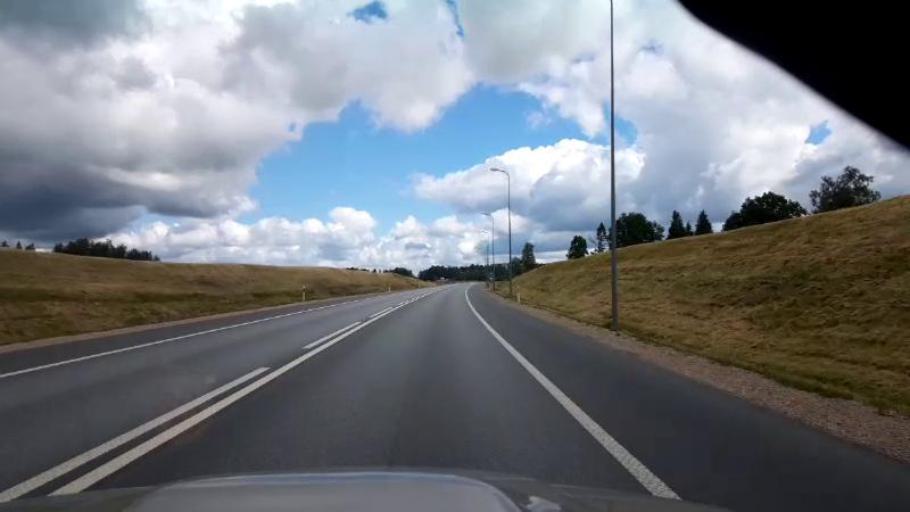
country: LV
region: Lecava
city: Iecava
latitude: 56.6342
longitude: 24.2242
